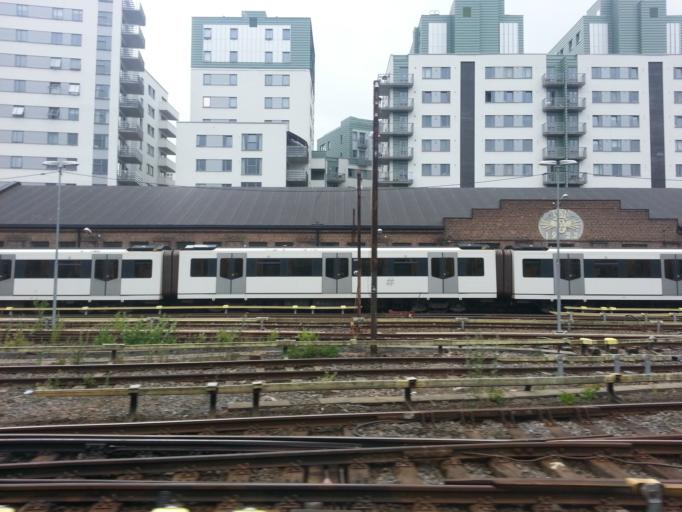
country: NO
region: Oslo
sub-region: Oslo
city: Sjolyststranda
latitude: 59.9317
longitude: 10.7124
